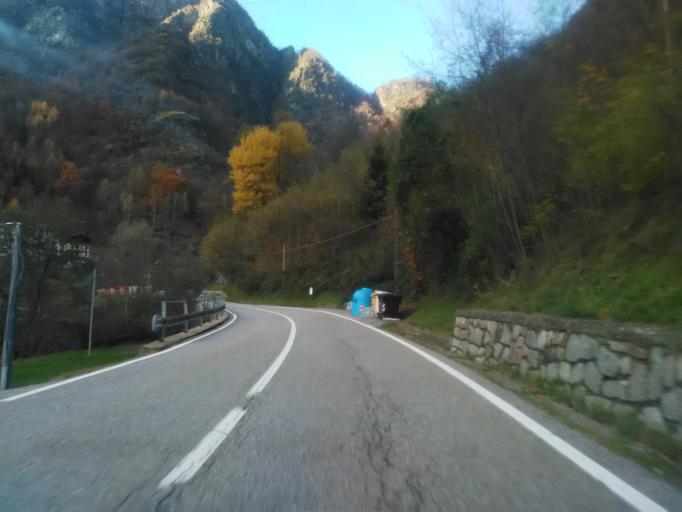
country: IT
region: Piedmont
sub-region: Provincia di Vercelli
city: Cravagliana
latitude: 45.8547
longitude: 8.1854
